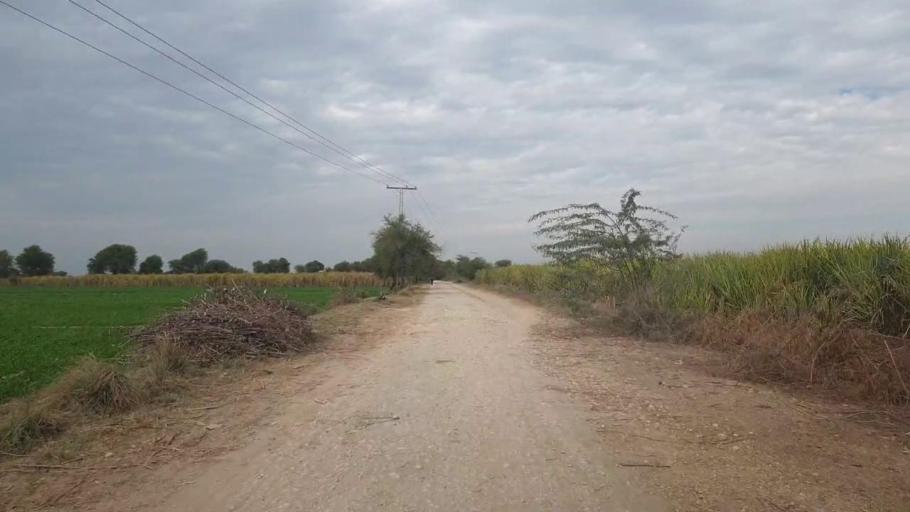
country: PK
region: Sindh
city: Jhol
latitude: 26.0195
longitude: 68.8750
